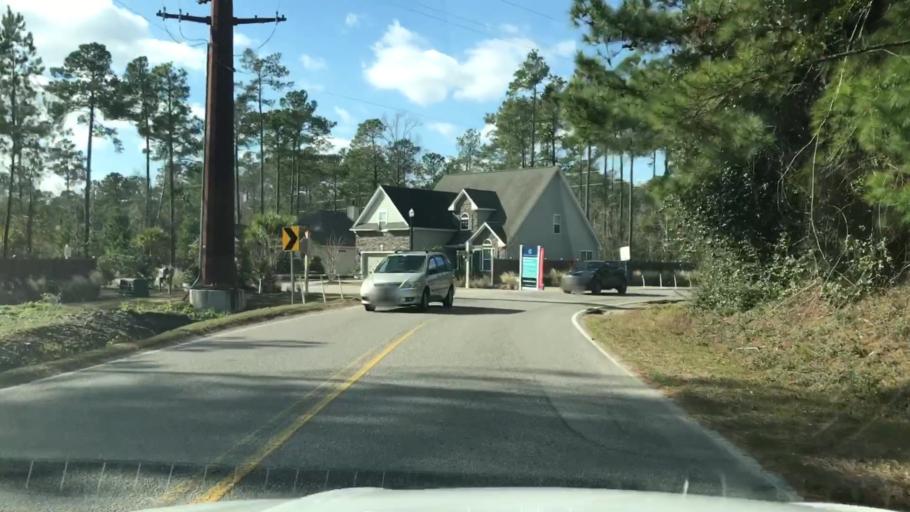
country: US
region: South Carolina
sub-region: Horry County
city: Socastee
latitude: 33.6579
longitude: -78.9984
